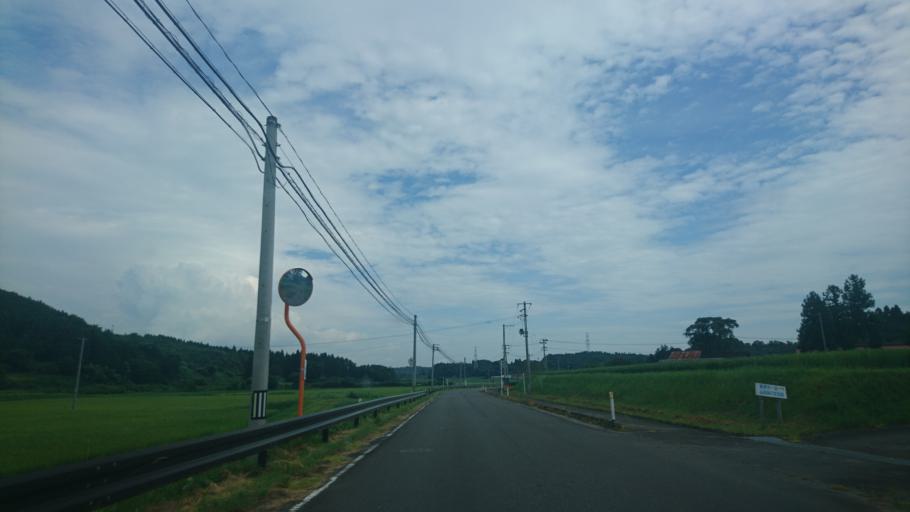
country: JP
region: Miyagi
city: Furukawa
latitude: 38.7665
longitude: 140.9651
